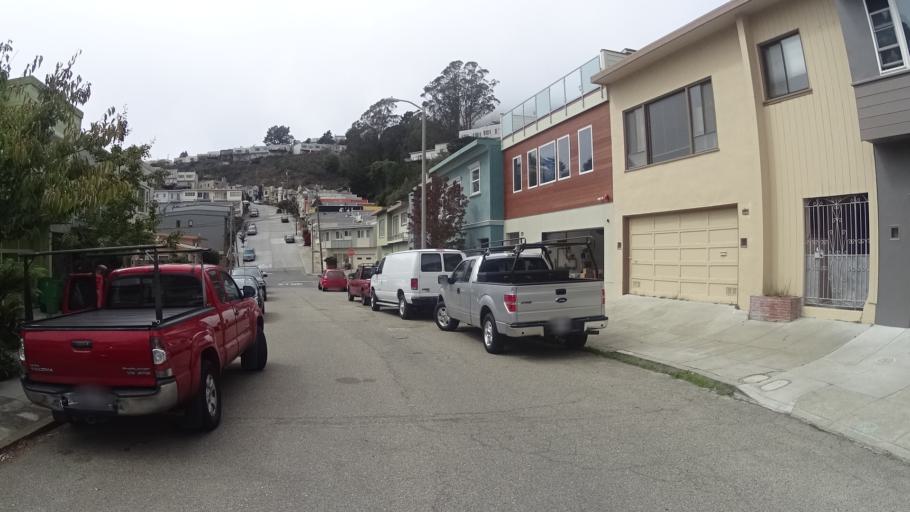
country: US
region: California
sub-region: San Mateo County
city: Daly City
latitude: 37.7360
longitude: -122.4481
